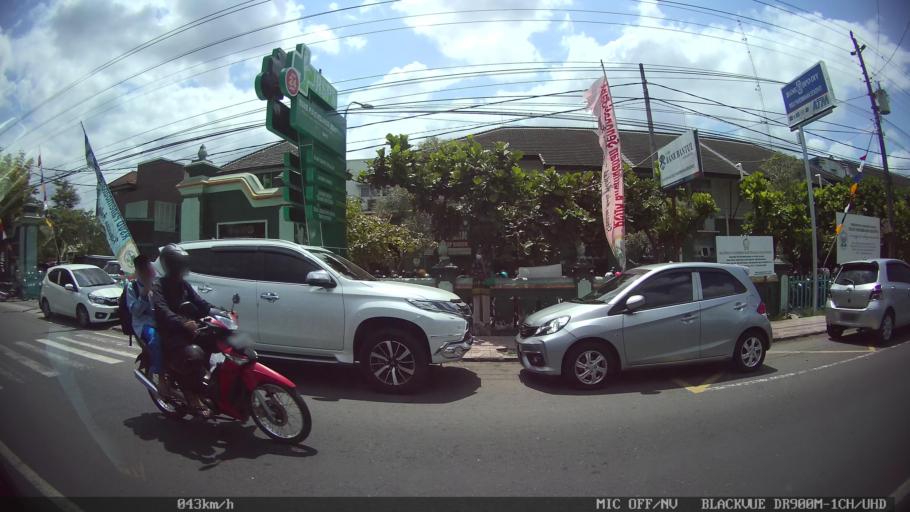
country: ID
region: Daerah Istimewa Yogyakarta
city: Bantul
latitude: -7.8932
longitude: 110.3384
